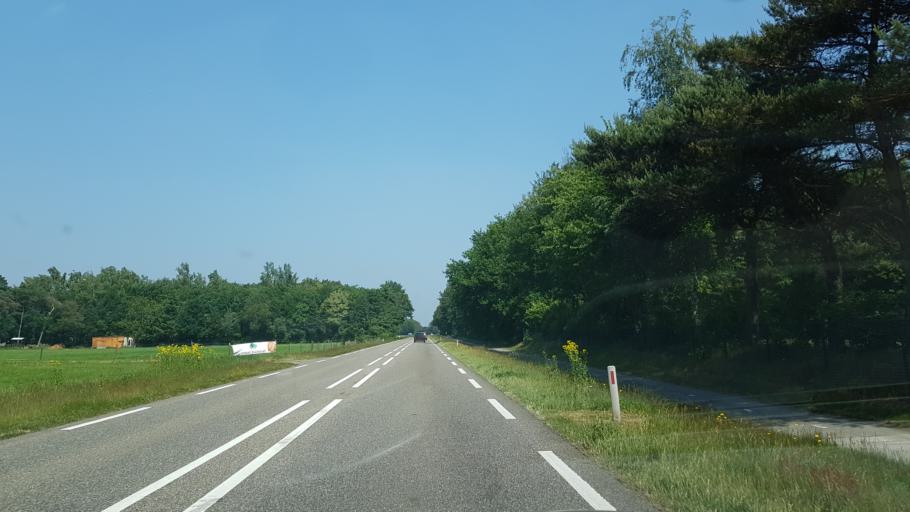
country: NL
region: Limburg
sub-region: Gemeente Peel en Maas
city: Maasbree
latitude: 51.3619
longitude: 5.9760
